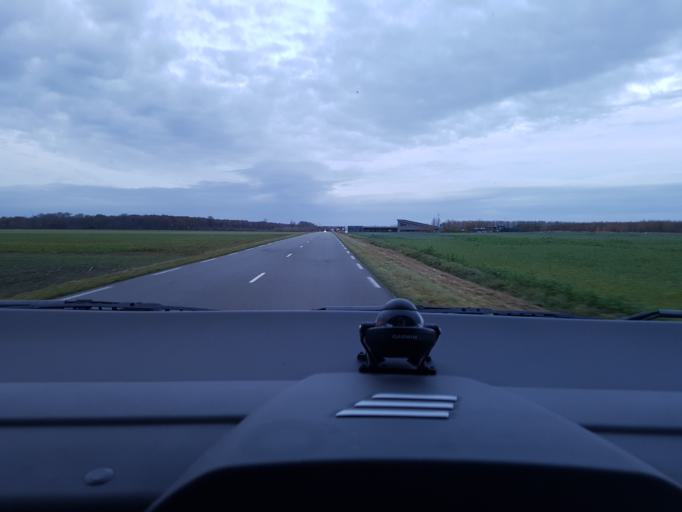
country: FR
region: Picardie
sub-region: Departement de la Somme
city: Poix-de-Picardie
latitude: 49.7588
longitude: 1.9704
